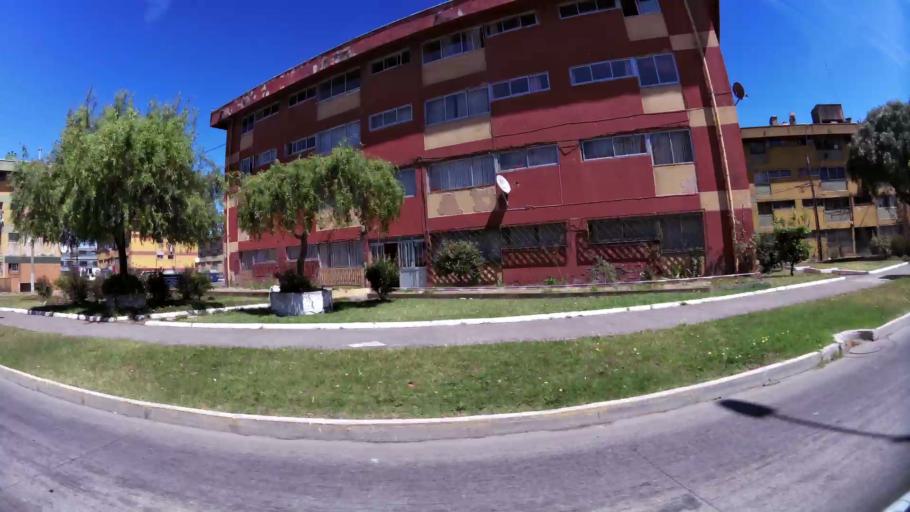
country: CL
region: Biobio
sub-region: Provincia de Concepcion
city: Talcahuano
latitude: -36.7242
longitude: -73.1067
